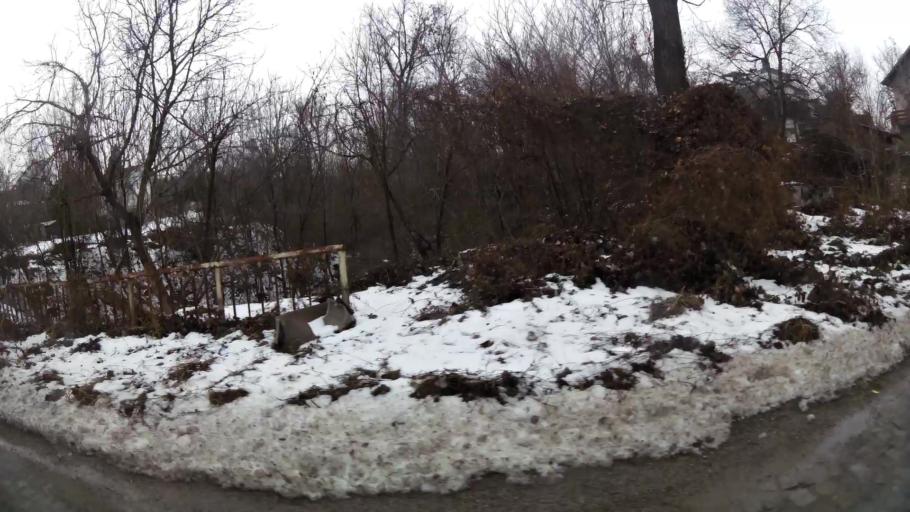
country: BG
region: Sofia-Capital
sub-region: Stolichna Obshtina
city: Sofia
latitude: 42.6707
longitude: 23.2401
